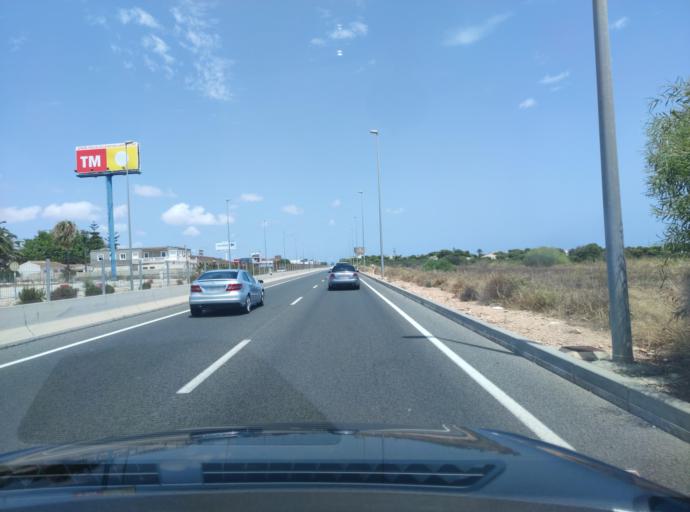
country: ES
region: Valencia
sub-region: Provincia de Alicante
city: Torrevieja
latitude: 37.9405
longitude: -0.7188
